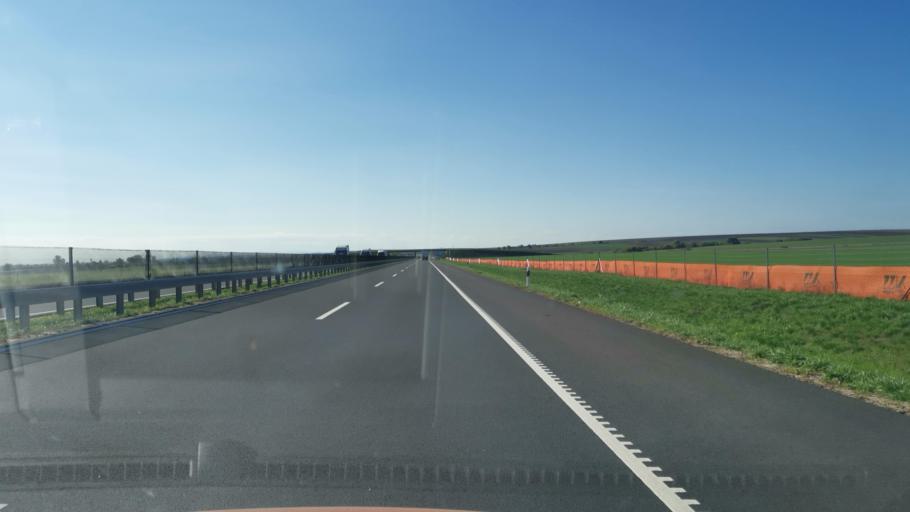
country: HU
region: Borsod-Abauj-Zemplen
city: Halmaj
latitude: 48.2976
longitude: 21.0486
